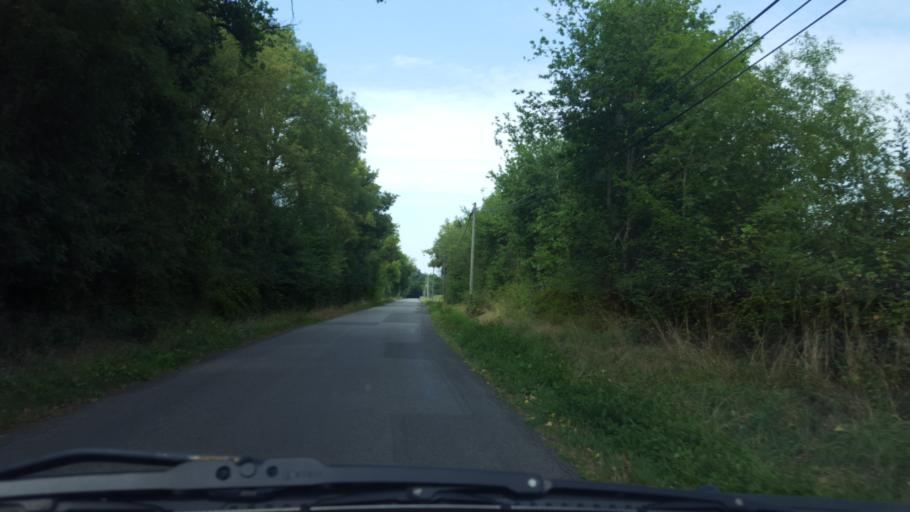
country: FR
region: Pays de la Loire
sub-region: Departement de la Loire-Atlantique
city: Saint-Philbert-de-Grand-Lieu
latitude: 47.0093
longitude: -1.6338
